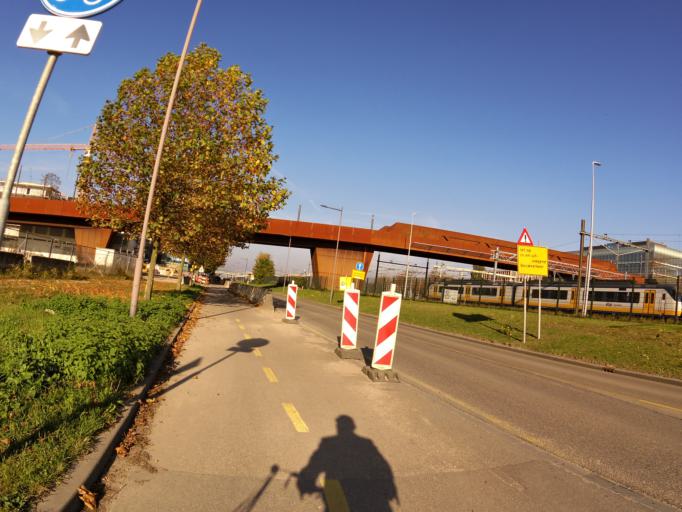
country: NL
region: North Brabant
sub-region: Gemeente 's-Hertogenbosch
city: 's-Hertogenbosch
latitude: 51.6843
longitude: 5.2901
